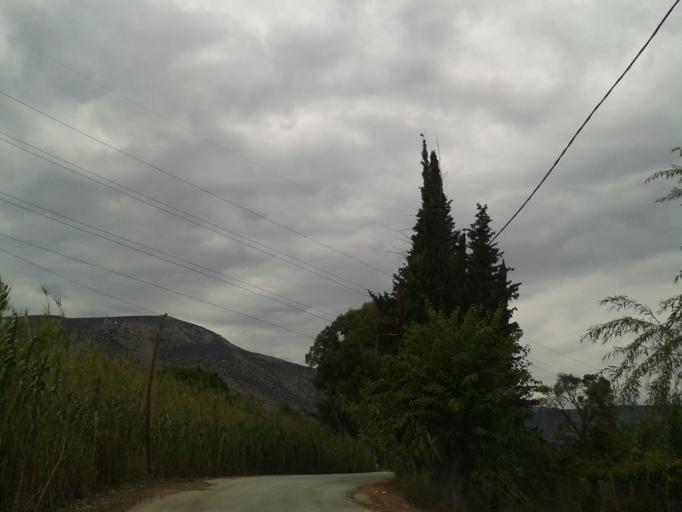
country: GR
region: Peloponnese
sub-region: Nomos Argolidos
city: Nea Kios
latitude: 37.5964
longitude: 22.7041
